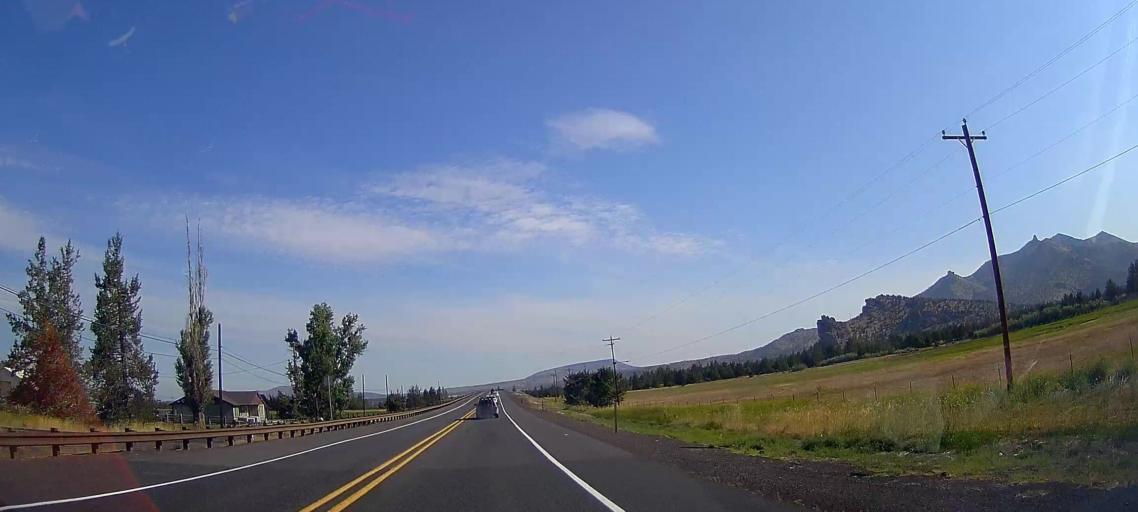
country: US
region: Oregon
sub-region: Deschutes County
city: Terrebonne
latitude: 44.3737
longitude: -121.1783
